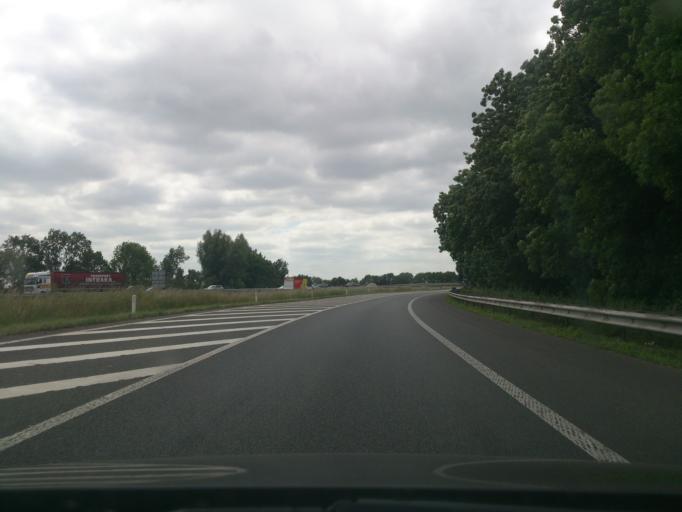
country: NL
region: Gelderland
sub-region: Gemeente Wijchen
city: Bergharen
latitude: 51.8100
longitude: 5.6769
